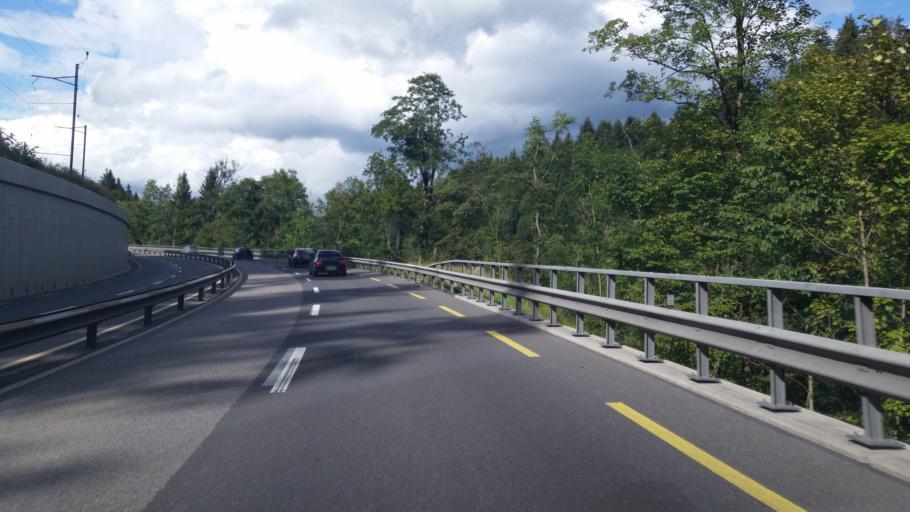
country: CH
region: Schwyz
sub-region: Bezirk Hoefe
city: Schindellegi
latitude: 47.1609
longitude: 8.7284
